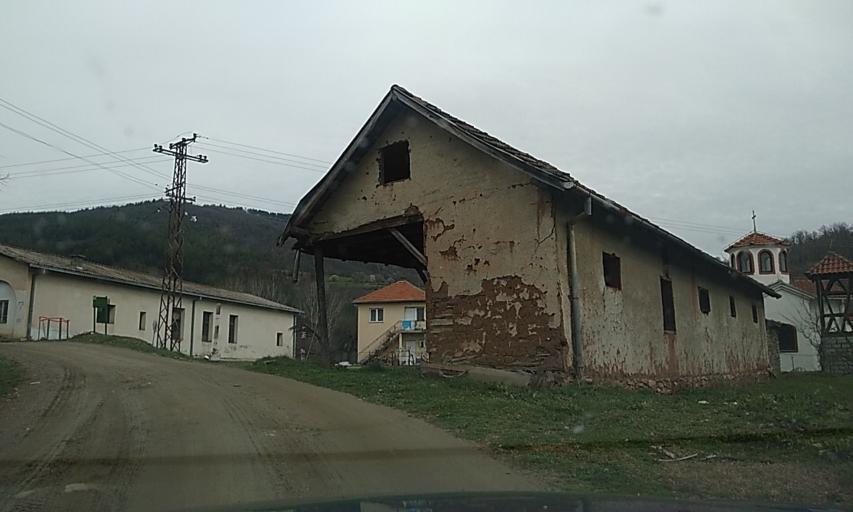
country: RS
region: Central Serbia
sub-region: Pcinjski Okrug
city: Bosilegrad
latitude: 42.3598
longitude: 22.4275
